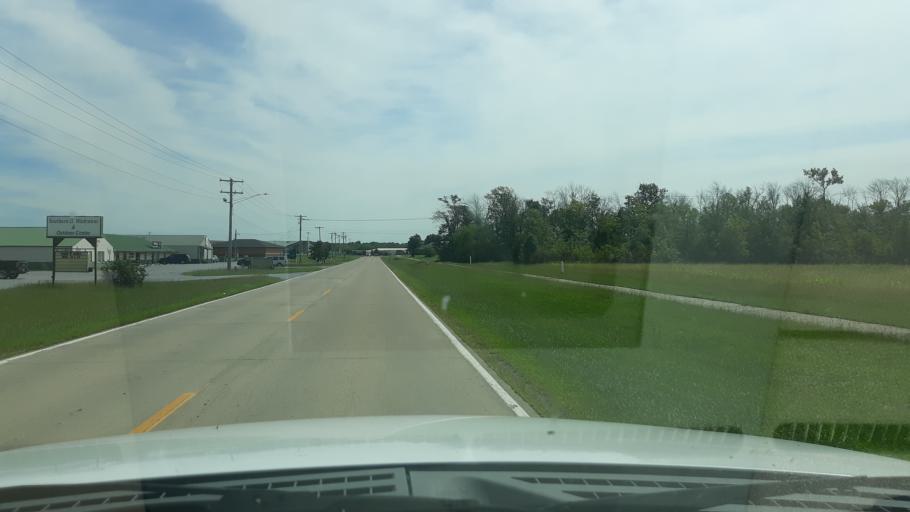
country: US
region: Illinois
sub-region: Saline County
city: Harrisburg
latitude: 37.7497
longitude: -88.5339
